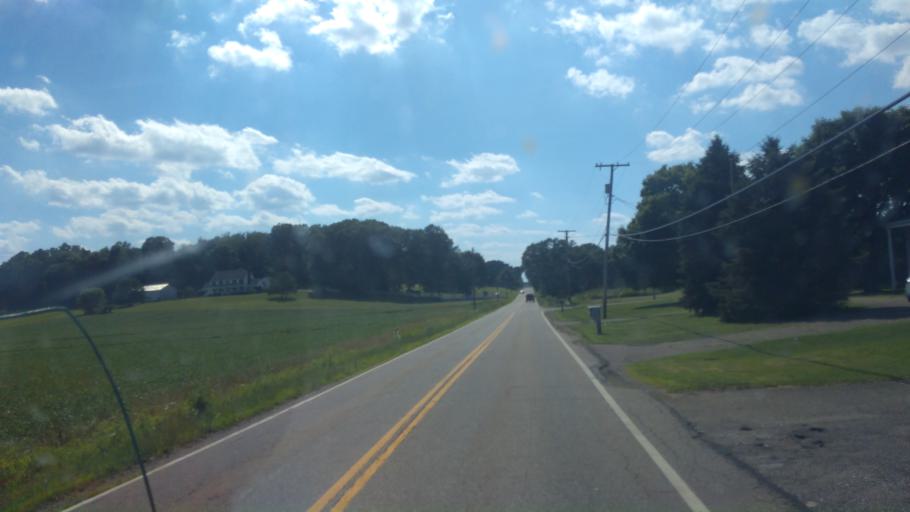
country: US
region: Ohio
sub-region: Stark County
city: Richville
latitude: 40.7306
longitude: -81.4615
